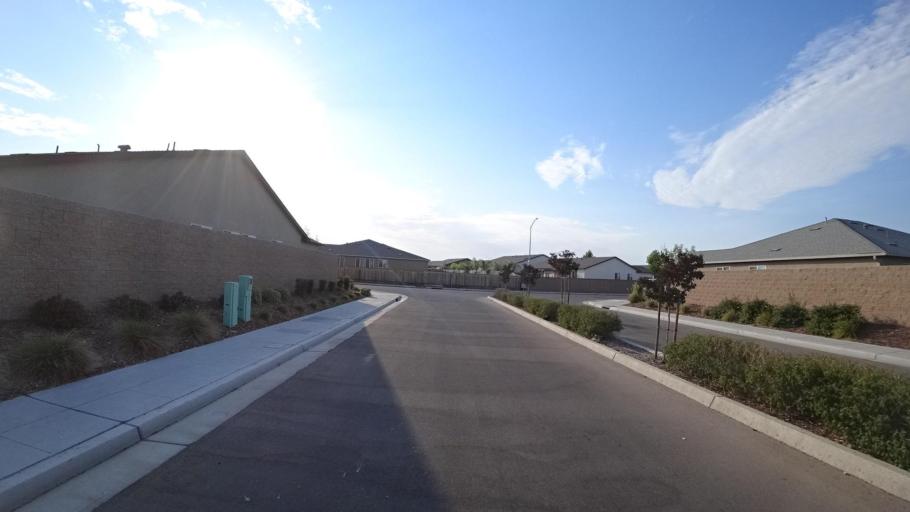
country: US
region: California
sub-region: Fresno County
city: Sunnyside
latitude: 36.7128
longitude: -119.7086
